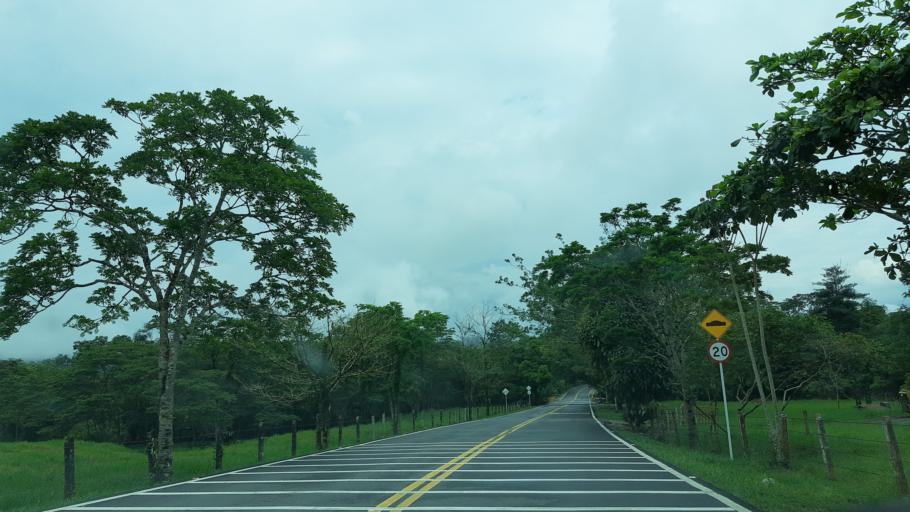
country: CO
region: Casanare
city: Sabanalarga
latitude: 4.7960
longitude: -73.0570
